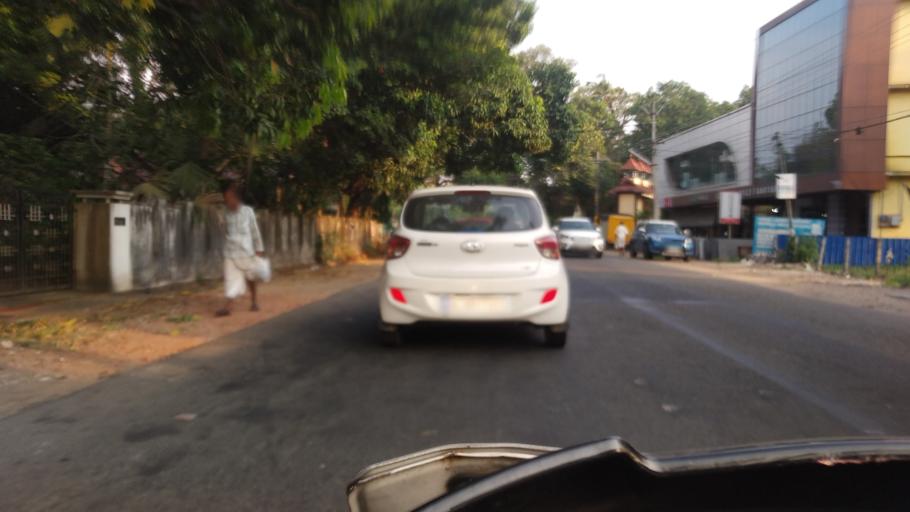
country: IN
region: Kerala
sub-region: Thrissur District
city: Irinjalakuda
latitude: 10.3137
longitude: 76.1481
